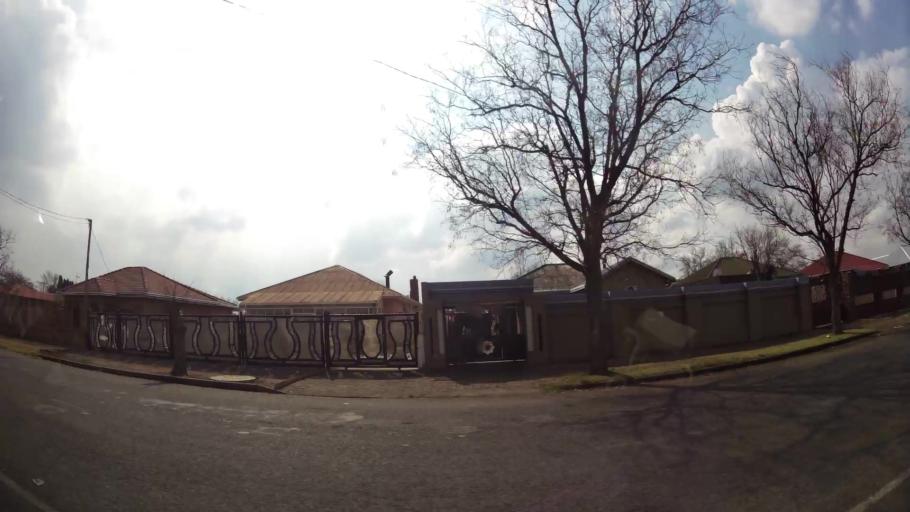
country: ZA
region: Gauteng
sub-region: Sedibeng District Municipality
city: Vereeniging
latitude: -26.6705
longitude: 27.9222
